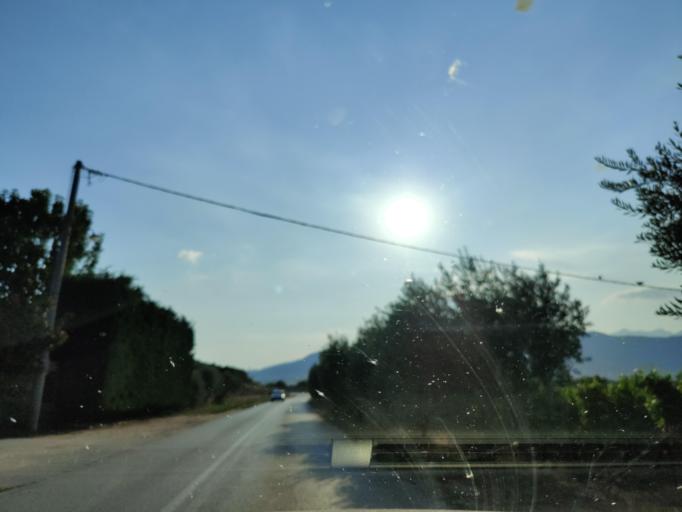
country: GR
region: East Macedonia and Thrace
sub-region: Nomos Kavalas
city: Nea Peramos
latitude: 40.8258
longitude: 24.2907
